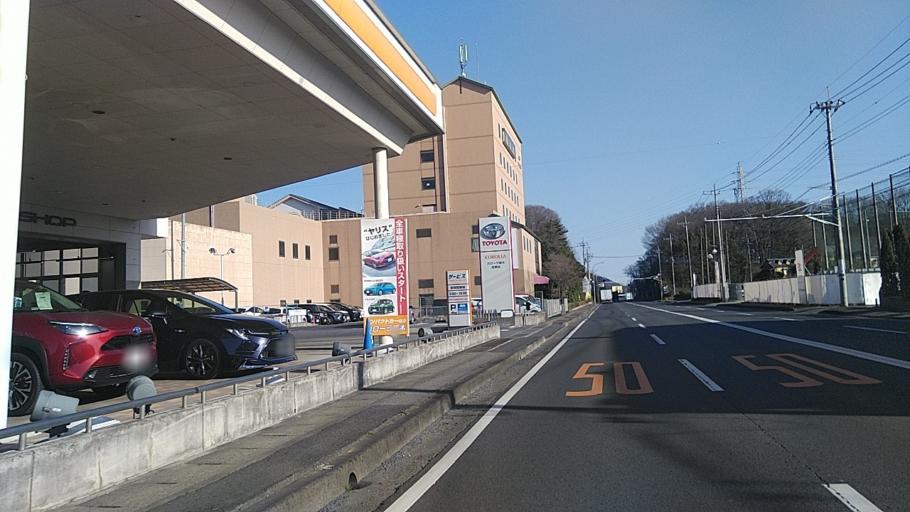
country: JP
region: Tochigi
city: Sano
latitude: 36.3326
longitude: 139.5836
